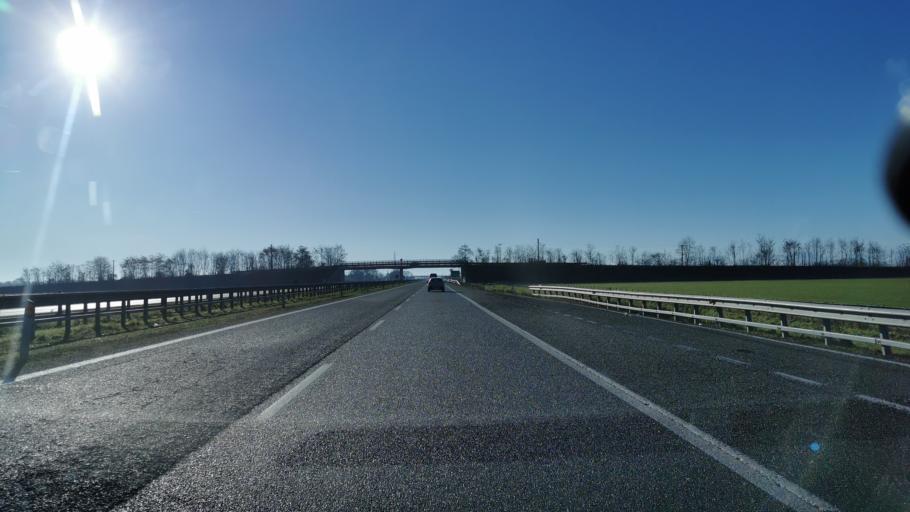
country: IT
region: Piedmont
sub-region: Provincia di Torino
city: Carmagnola
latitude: 44.8803
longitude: 7.7470
